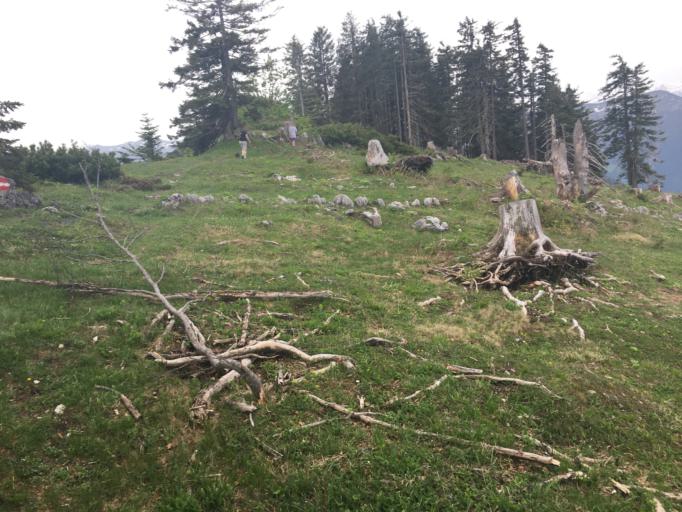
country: AT
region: Salzburg
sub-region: Politischer Bezirk Salzburg-Umgebung
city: Faistenau
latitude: 47.7474
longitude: 13.2036
